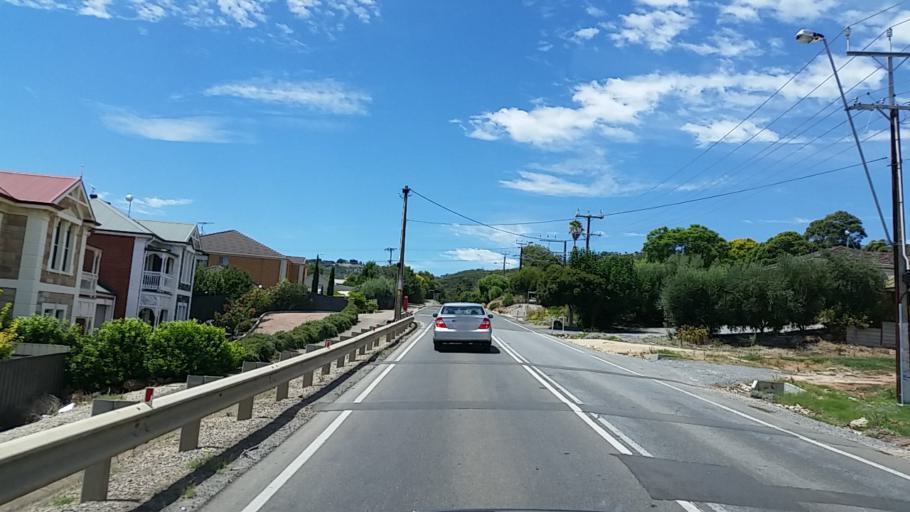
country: AU
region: South Australia
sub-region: Campbelltown
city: Athelstone
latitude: -34.8647
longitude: 138.7104
